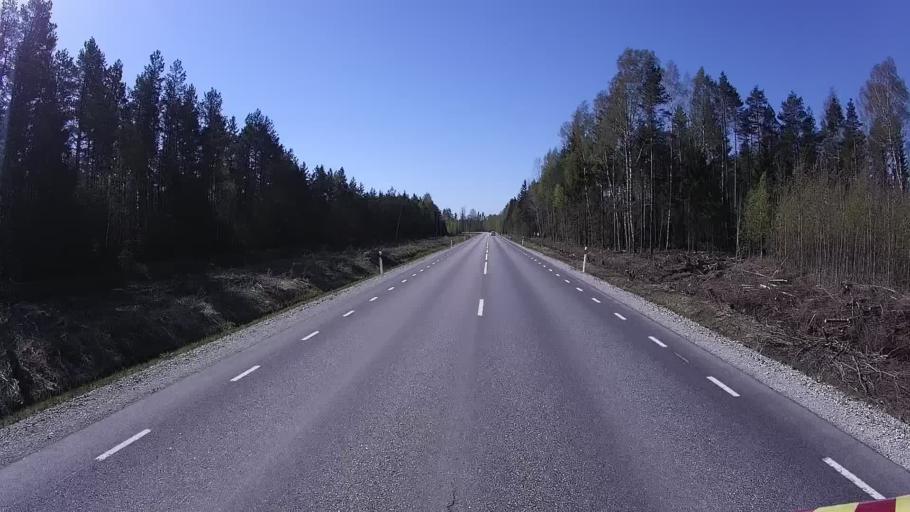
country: EE
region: Raplamaa
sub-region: Jaervakandi vald
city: Jarvakandi
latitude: 58.7616
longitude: 24.8142
